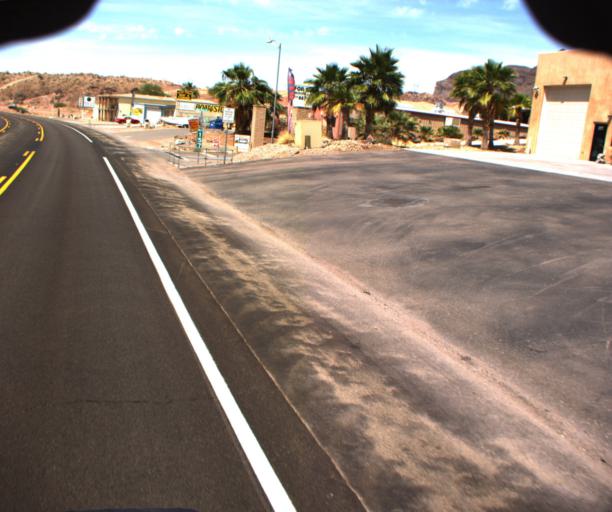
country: US
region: Arizona
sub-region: La Paz County
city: Cienega Springs
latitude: 34.2621
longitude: -114.1294
